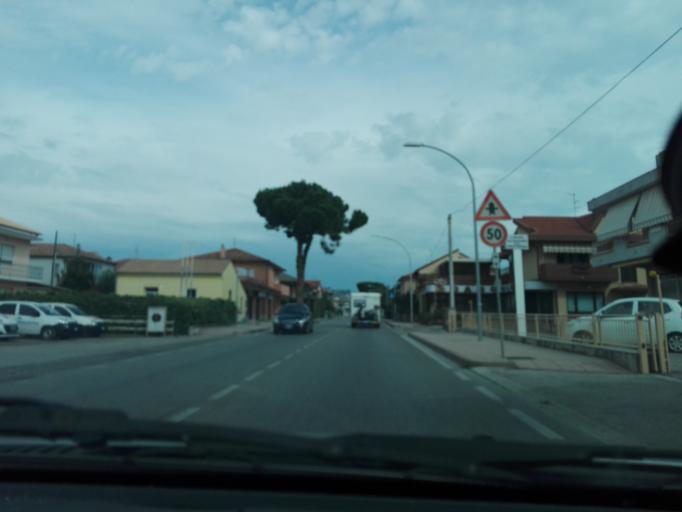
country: IT
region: Abruzzo
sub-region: Provincia di Pescara
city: San Martino Bassa
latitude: 42.5262
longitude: 14.1382
